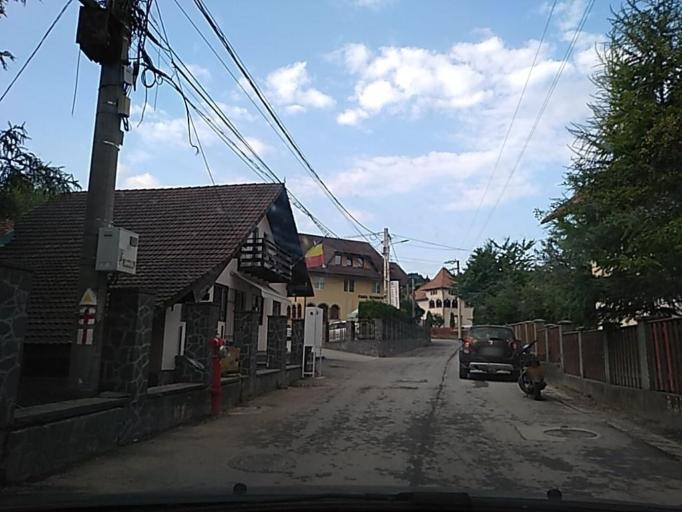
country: RO
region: Brasov
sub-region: Comuna Bran
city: Simon
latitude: 45.5003
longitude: 25.3840
